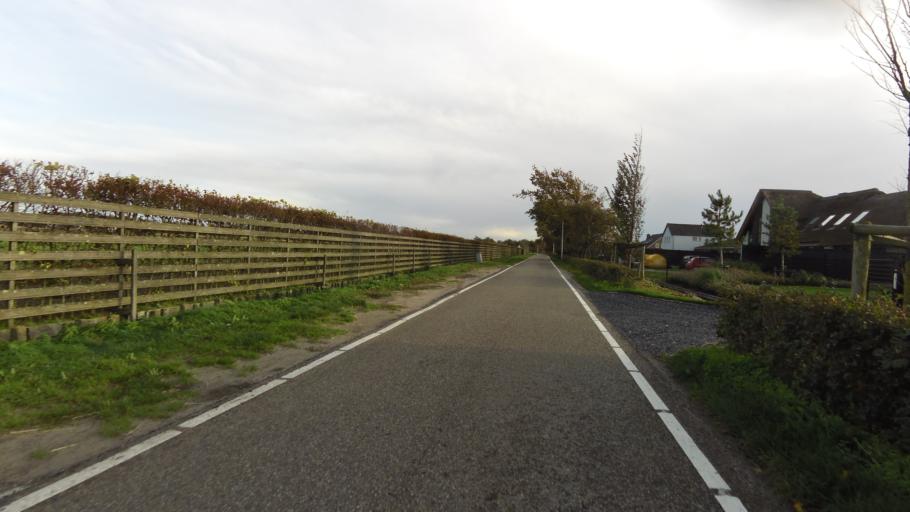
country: NL
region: South Holland
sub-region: Gemeente Noordwijkerhout
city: Noordwijkerhout
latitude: 52.2869
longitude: 4.4984
